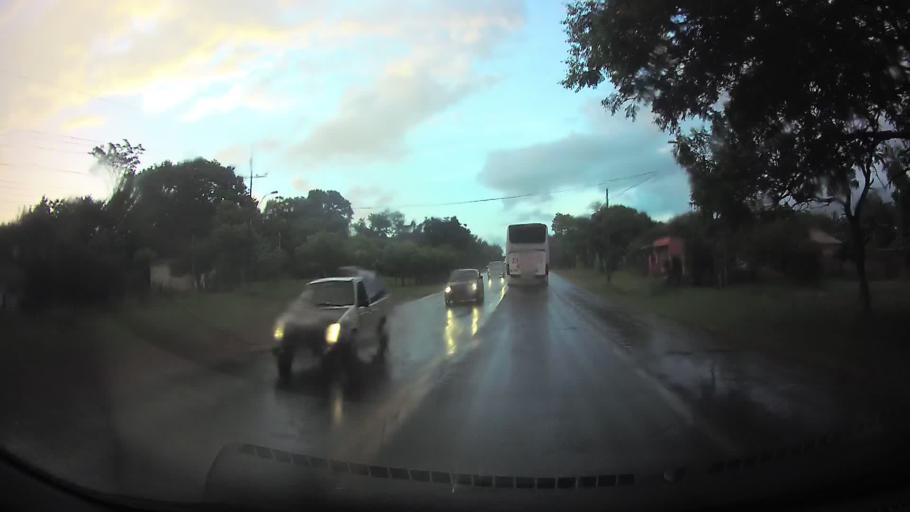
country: PY
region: Paraguari
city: Yaguaron
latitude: -25.5817
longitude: -57.2509
